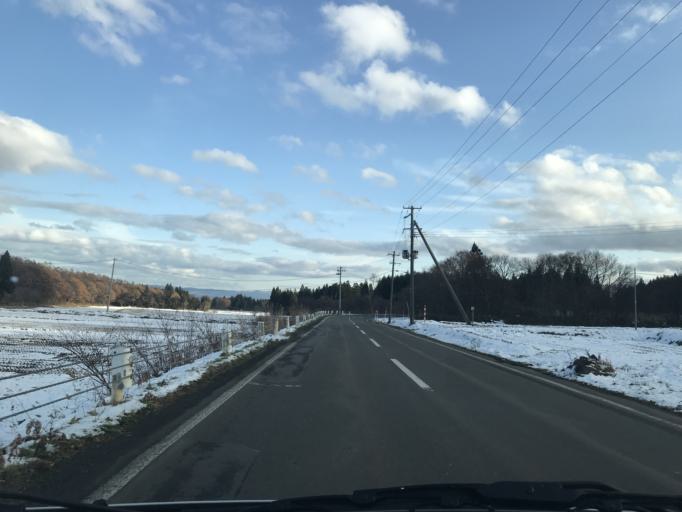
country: JP
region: Iwate
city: Kitakami
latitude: 39.2319
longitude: 141.0090
